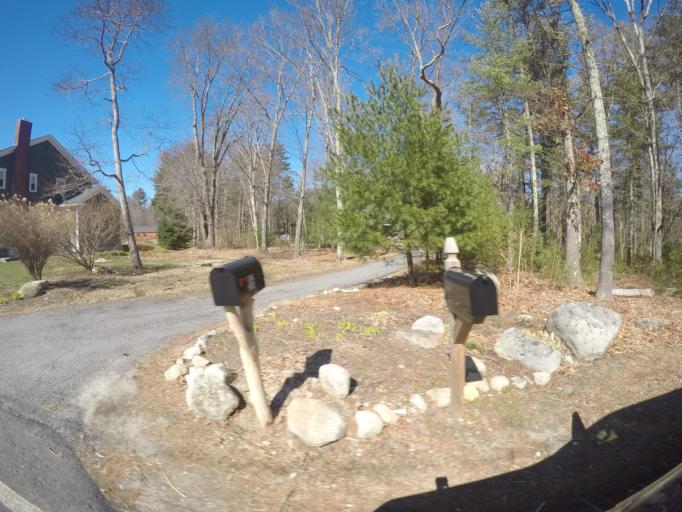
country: US
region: Massachusetts
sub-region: Bristol County
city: Easton
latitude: 42.0084
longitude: -71.1095
